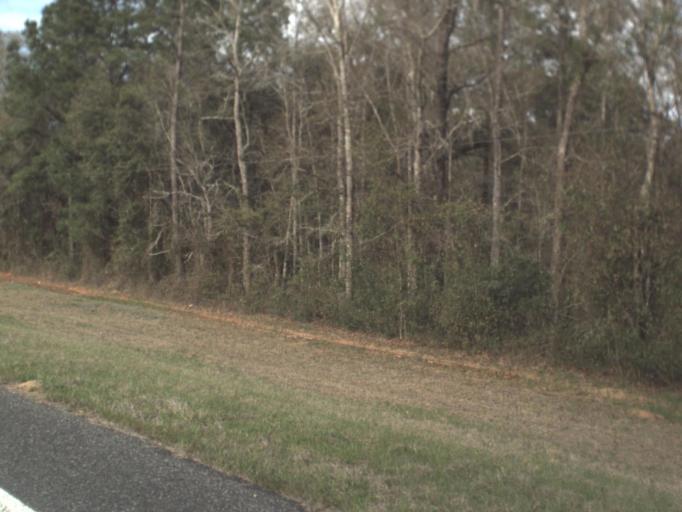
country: US
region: Florida
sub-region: Jefferson County
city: Monticello
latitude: 30.6351
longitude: -83.8731
